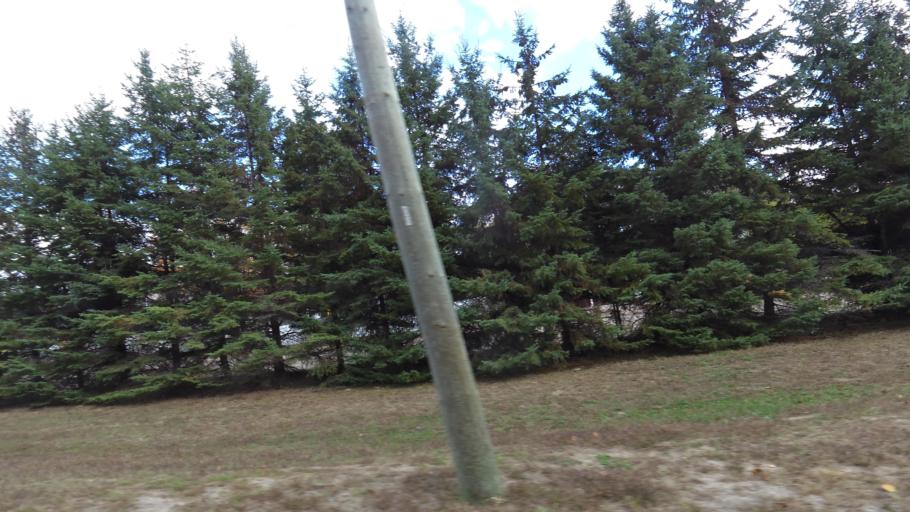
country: CA
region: Ontario
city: Deep River
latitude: 46.0953
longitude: -77.4846
